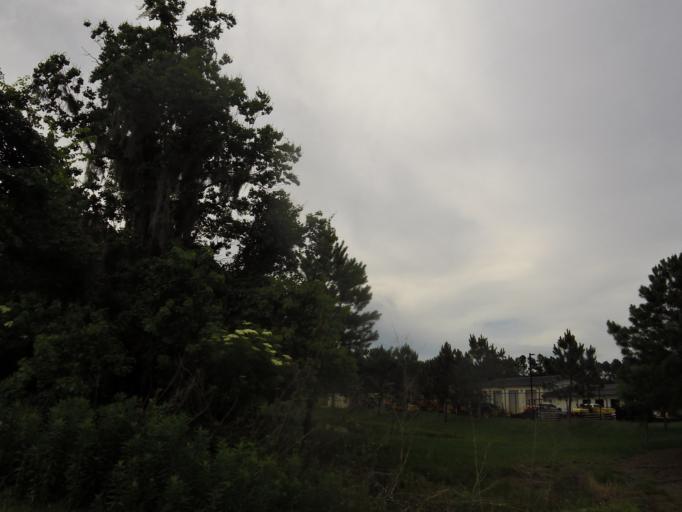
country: US
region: Florida
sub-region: Nassau County
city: Nassau Village-Ratliff
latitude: 30.5471
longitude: -81.7241
